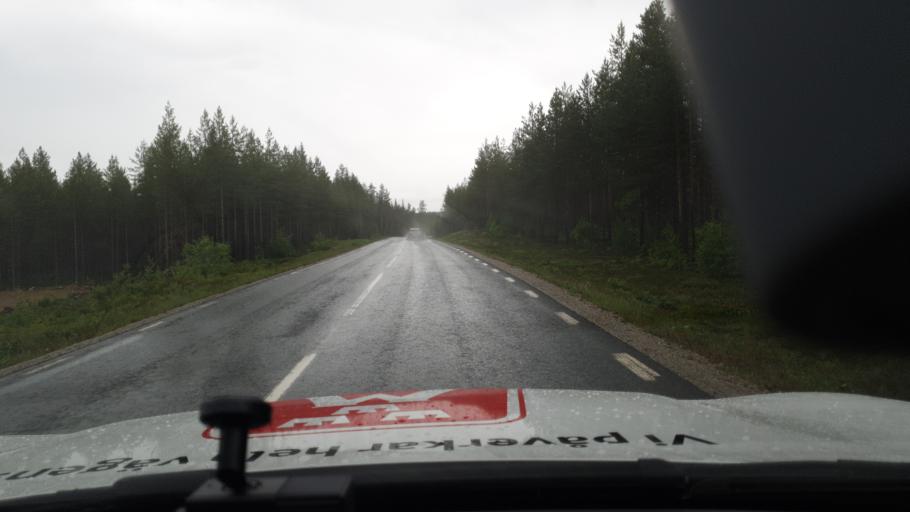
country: SE
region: Vaesterbotten
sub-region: Lycksele Kommun
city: Lycksele
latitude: 64.4849
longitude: 18.8987
